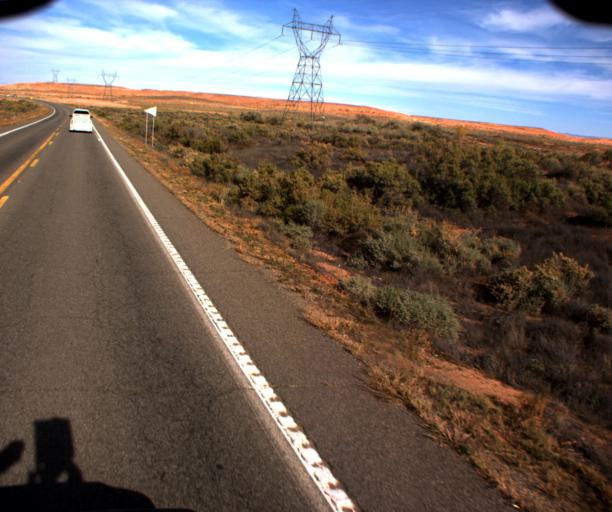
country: US
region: Arizona
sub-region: Navajo County
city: Kayenta
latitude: 36.8455
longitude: -109.8373
